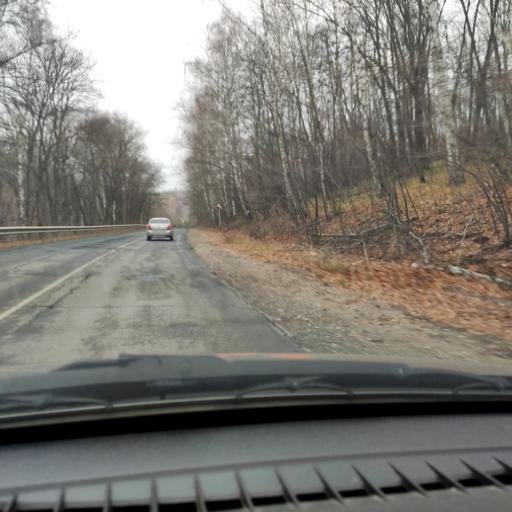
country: RU
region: Samara
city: Zhigulevsk
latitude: 53.4262
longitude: 49.6598
